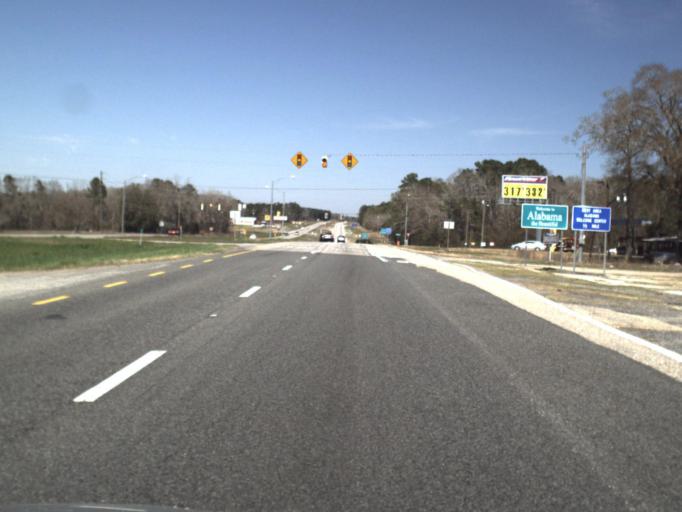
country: US
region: Alabama
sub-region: Houston County
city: Cottonwood
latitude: 30.9978
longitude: -85.4075
